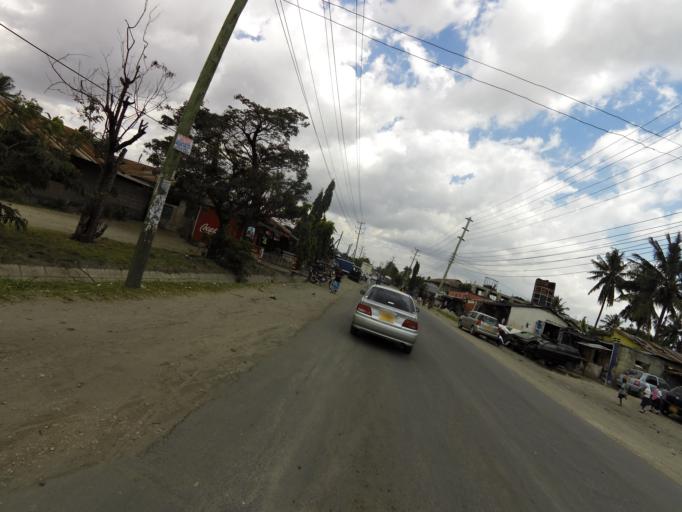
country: TZ
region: Dar es Salaam
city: Magomeni
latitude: -6.7909
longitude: 39.2358
